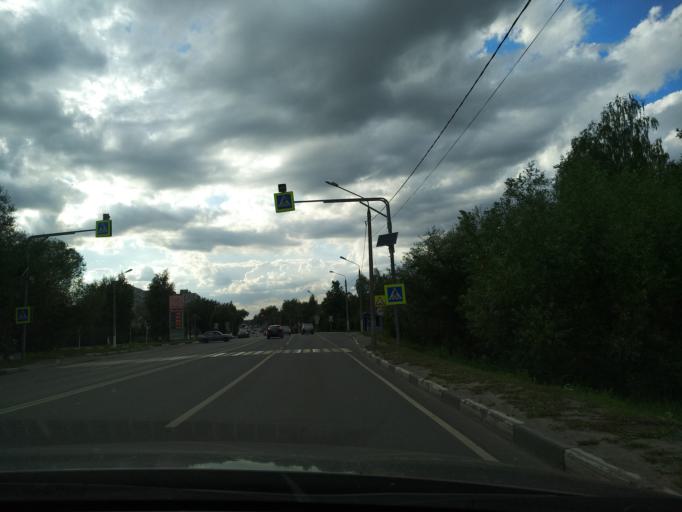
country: RU
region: Moskovskaya
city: Yegor'yevsk
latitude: 55.3668
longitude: 39.0735
